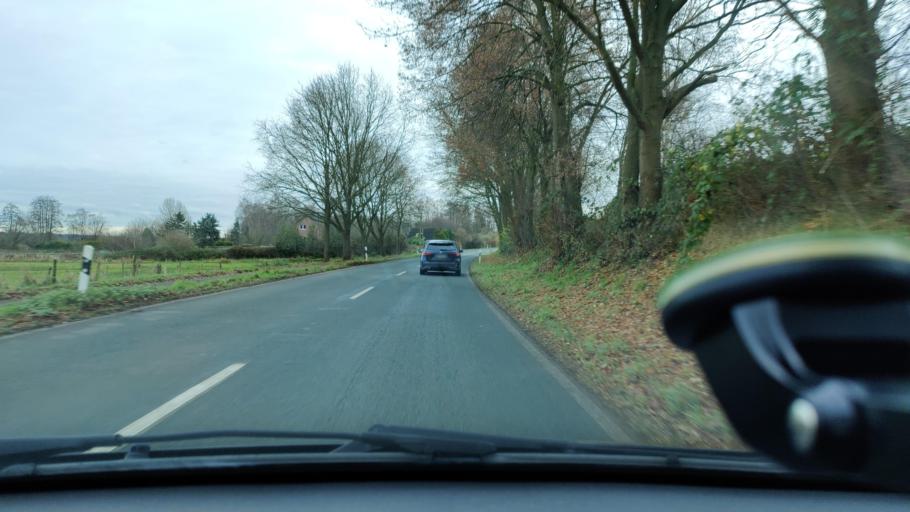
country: DE
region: North Rhine-Westphalia
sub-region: Regierungsbezirk Dusseldorf
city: Sonsbeck
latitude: 51.6286
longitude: 6.4139
